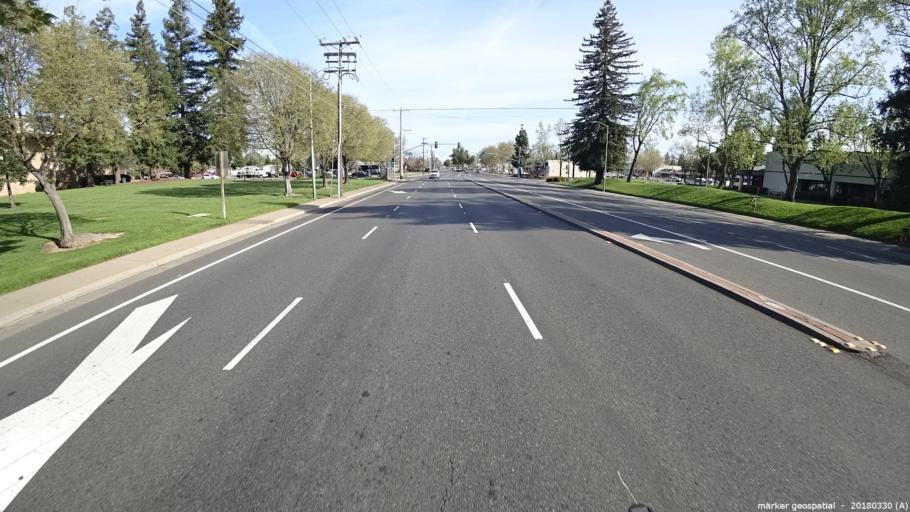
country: US
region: California
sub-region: Sacramento County
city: La Riviera
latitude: 38.5539
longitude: -121.3363
